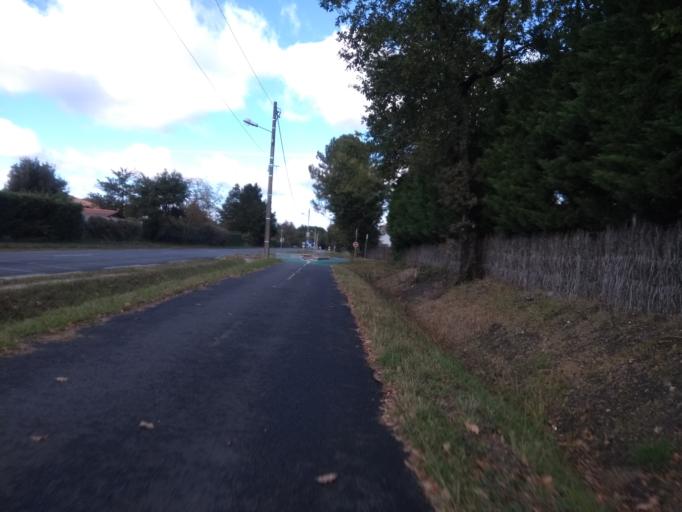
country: FR
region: Aquitaine
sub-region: Departement de la Gironde
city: Saint-Aubin-de-Medoc
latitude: 44.7954
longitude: -0.7049
